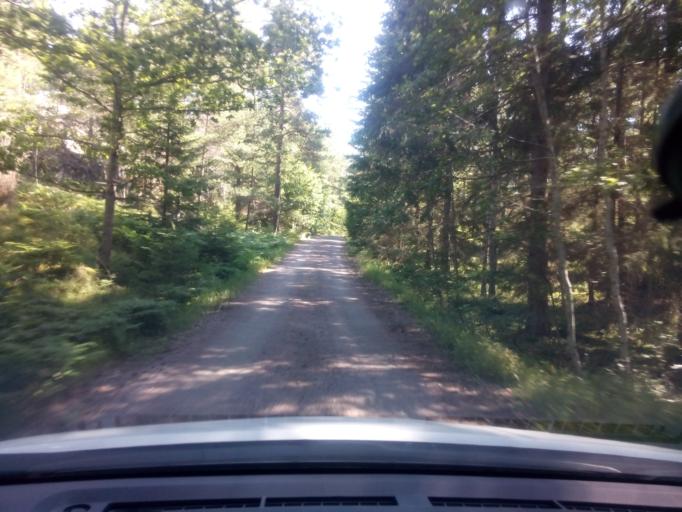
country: SE
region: Soedermanland
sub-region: Oxelosunds Kommun
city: Oxelosund
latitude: 58.7304
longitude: 17.2349
